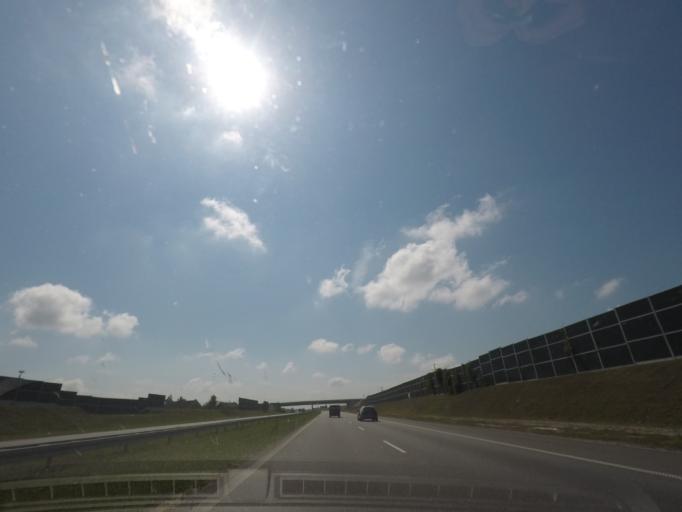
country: PL
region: Kujawsko-Pomorskie
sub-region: Powiat wloclawski
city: Czerniewice
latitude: 52.5042
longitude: 19.1173
